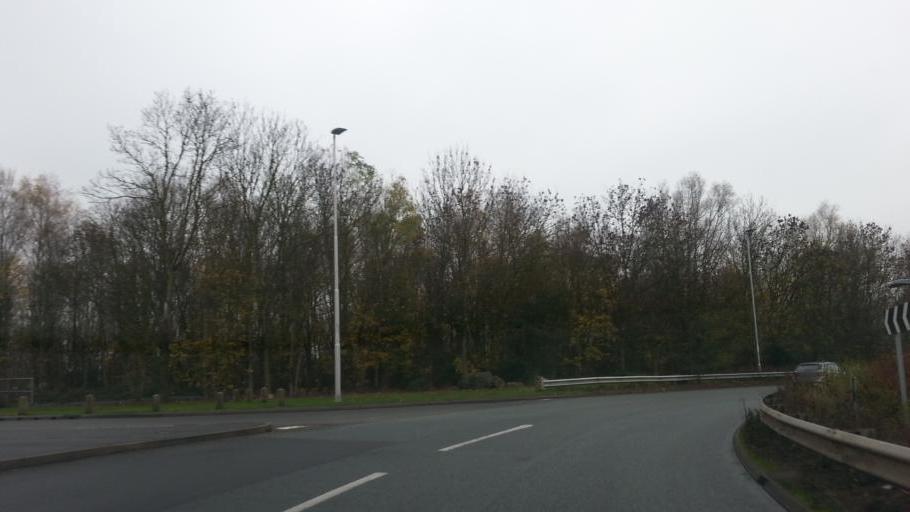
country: GB
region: England
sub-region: Cambridgeshire
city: Yaxley
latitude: 52.5359
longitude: -0.3025
